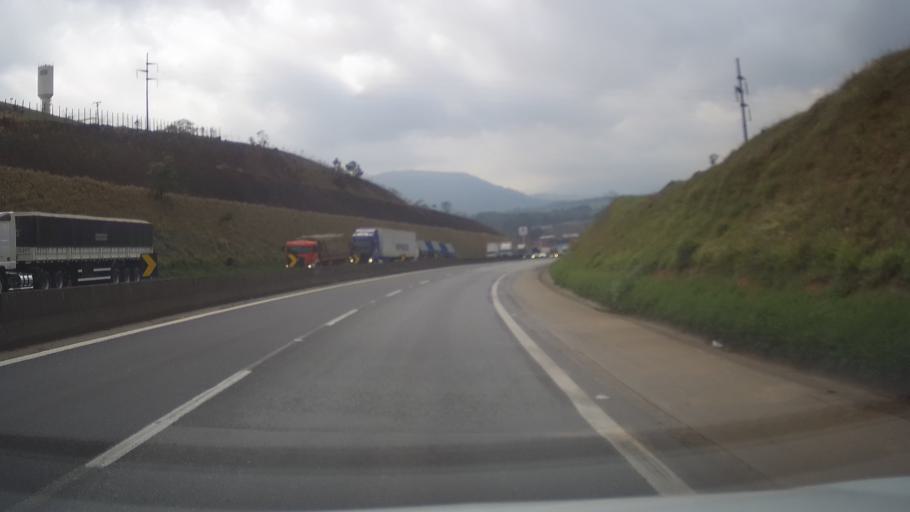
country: BR
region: Minas Gerais
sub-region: Extrema
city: Extrema
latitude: -22.8352
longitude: -46.3244
